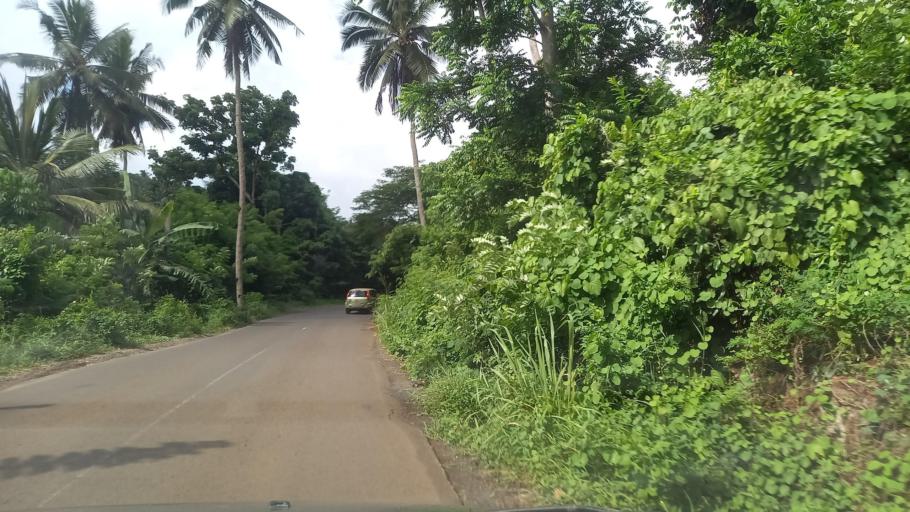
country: YT
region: Ouangani
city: Ouangani
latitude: -12.8410
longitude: 45.1240
